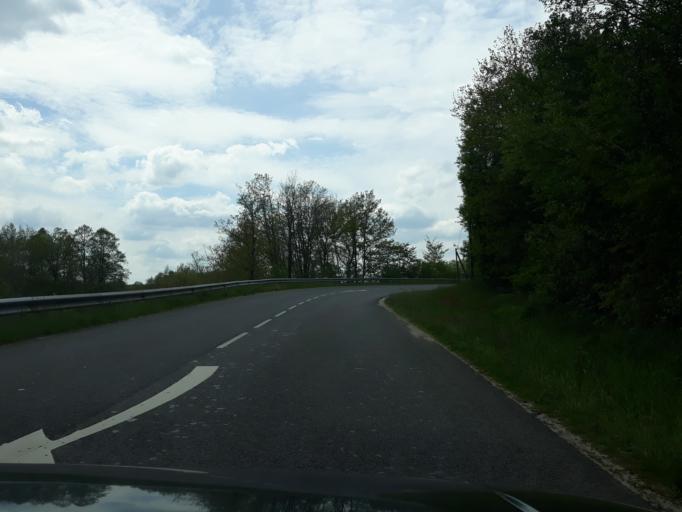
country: FR
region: Lorraine
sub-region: Departement des Vosges
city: Bruyeres
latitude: 48.1860
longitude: 6.7474
